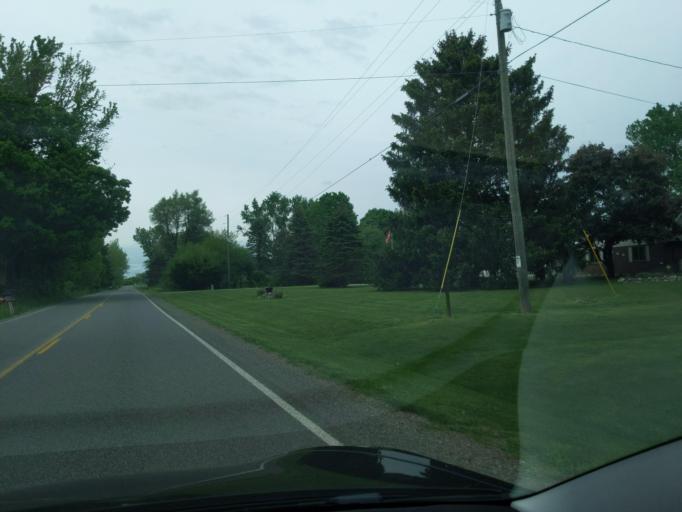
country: US
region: Michigan
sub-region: Ingham County
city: Leslie
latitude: 42.5043
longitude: -84.4269
